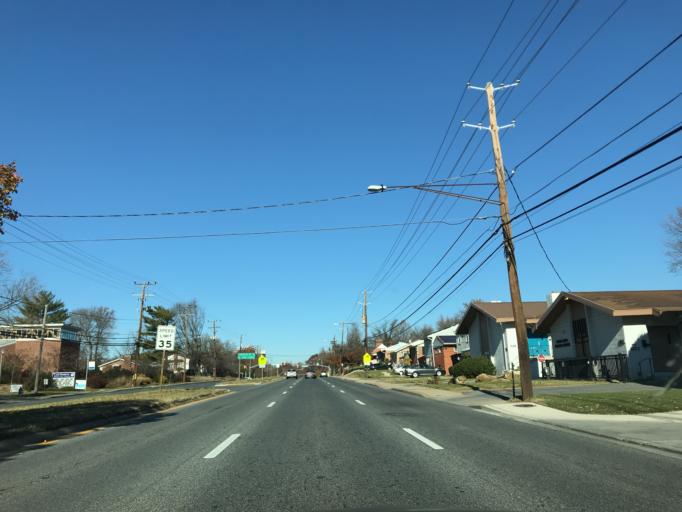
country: US
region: Maryland
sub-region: Montgomery County
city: Kemp Mill
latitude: 39.0317
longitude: -77.0224
